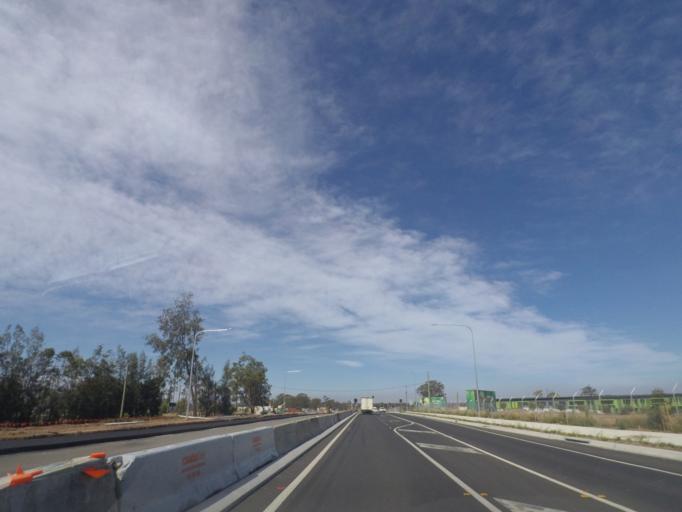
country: AU
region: New South Wales
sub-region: Campbelltown Municipality
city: Denham Court
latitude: -33.9752
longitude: 150.8552
